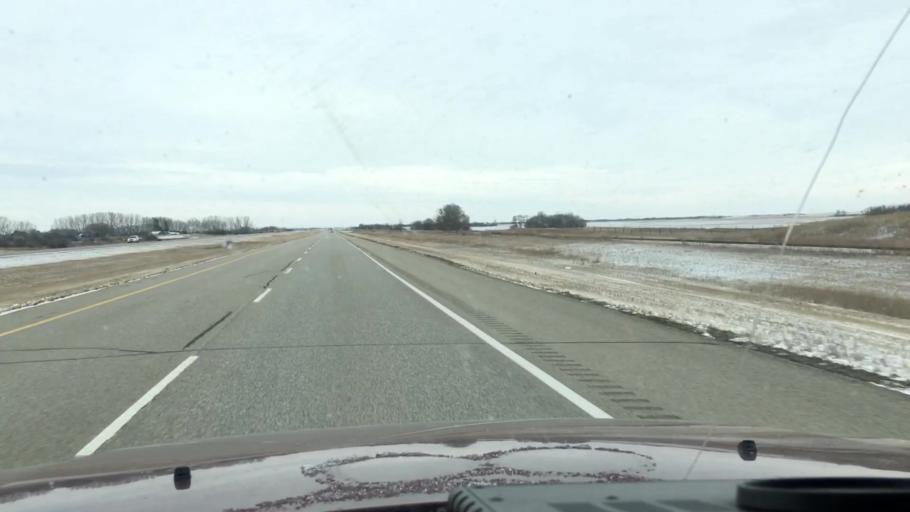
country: CA
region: Saskatchewan
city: Watrous
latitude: 51.3460
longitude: -106.1084
